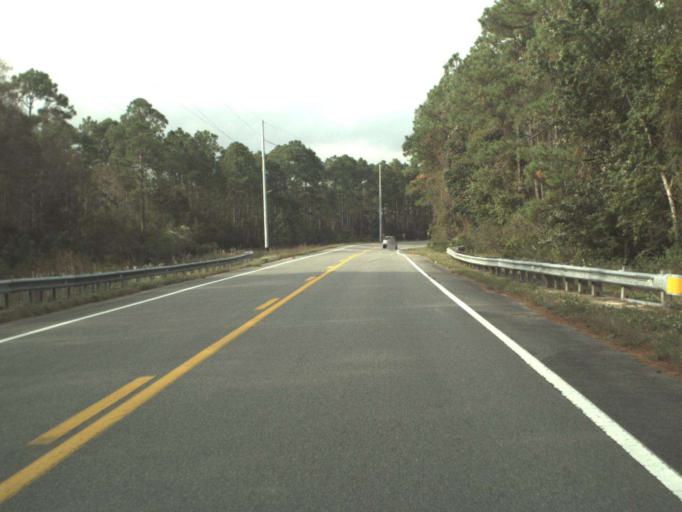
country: US
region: Florida
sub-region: Franklin County
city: Carrabelle
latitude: 29.9538
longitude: -84.5047
